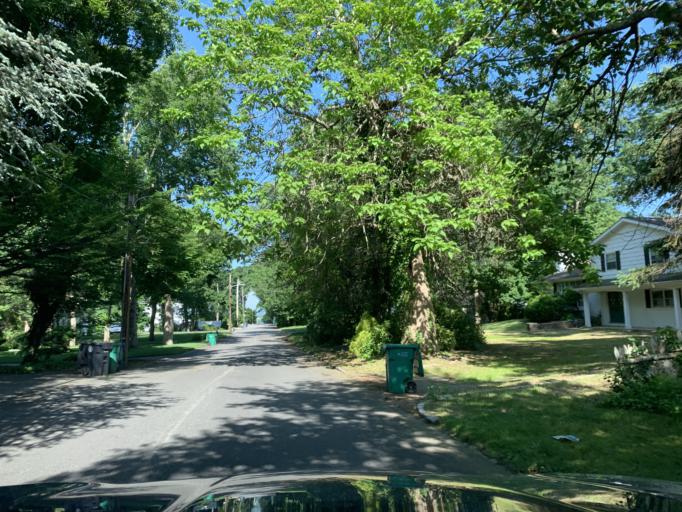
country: US
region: Rhode Island
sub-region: Kent County
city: East Greenwich
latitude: 41.6825
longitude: -71.4568
